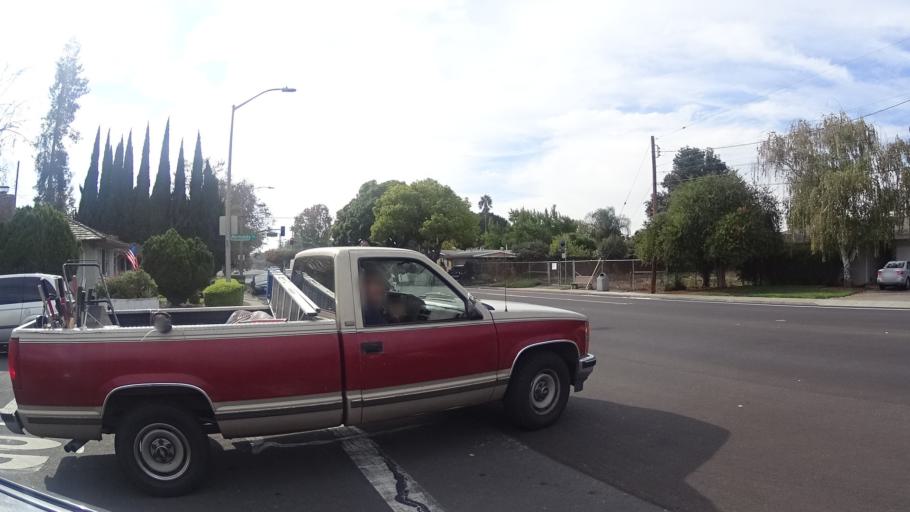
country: US
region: California
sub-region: Santa Clara County
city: Burbank
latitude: 37.3385
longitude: -121.9434
